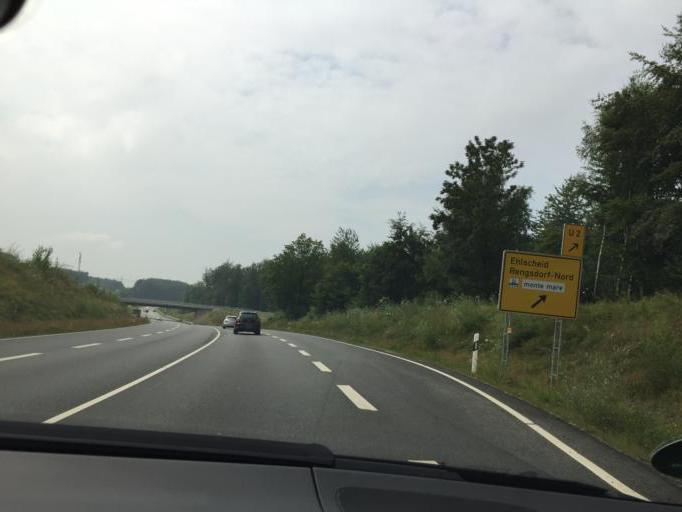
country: DE
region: Rheinland-Pfalz
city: Rengsdorf
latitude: 50.5160
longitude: 7.4835
